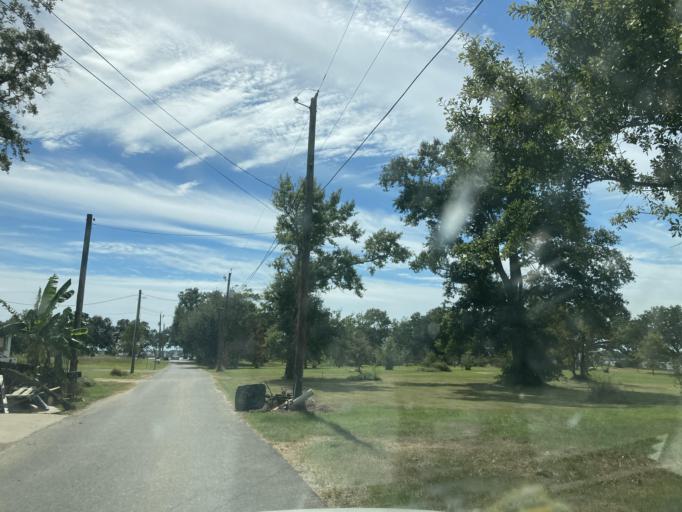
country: US
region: Mississippi
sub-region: Harrison County
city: D'Iberville
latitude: 30.4265
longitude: -88.8812
